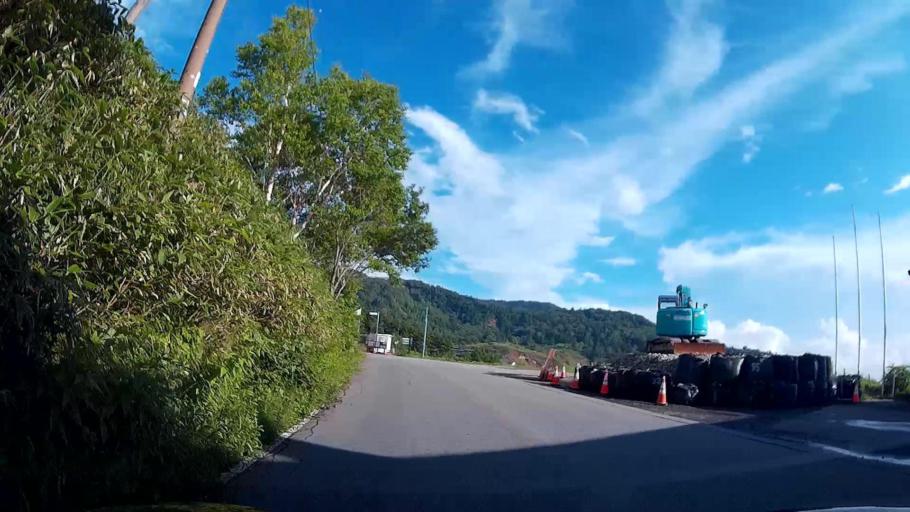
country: JP
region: Nagano
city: Nakano
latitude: 36.6386
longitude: 138.5107
